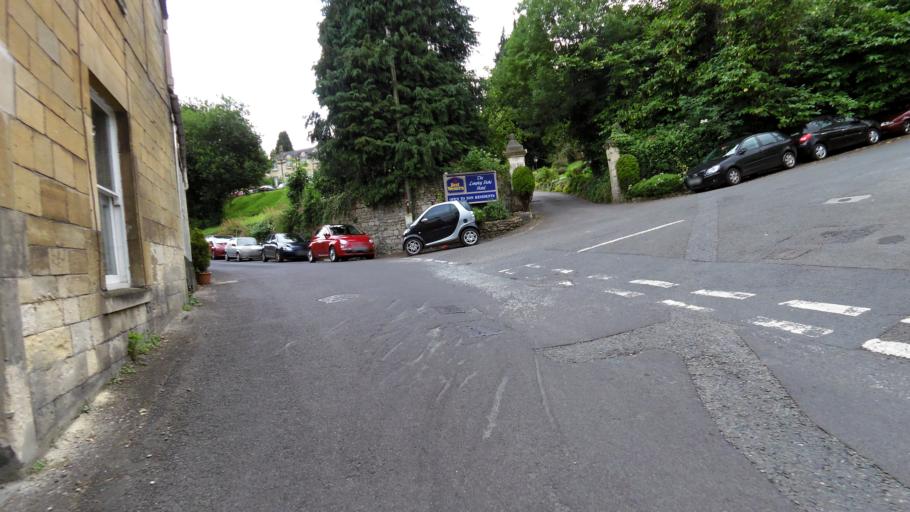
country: GB
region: England
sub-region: Bath and North East Somerset
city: Freshford
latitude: 51.3333
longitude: -2.3000
